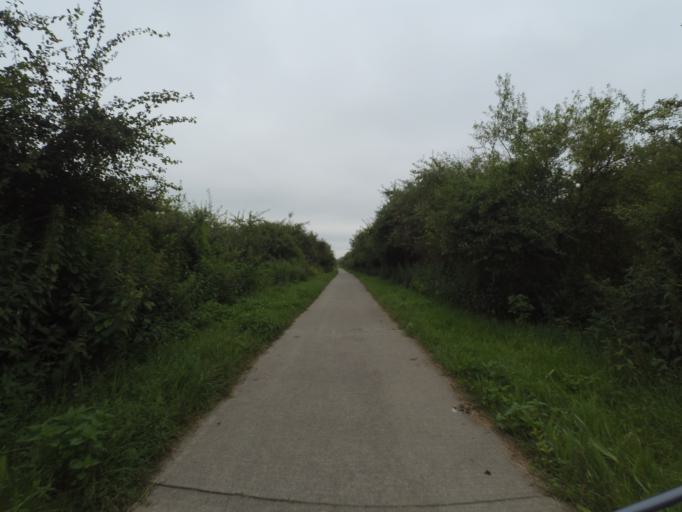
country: NL
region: Flevoland
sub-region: Gemeente Almere
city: Almere Stad
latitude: 52.4248
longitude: 5.2729
